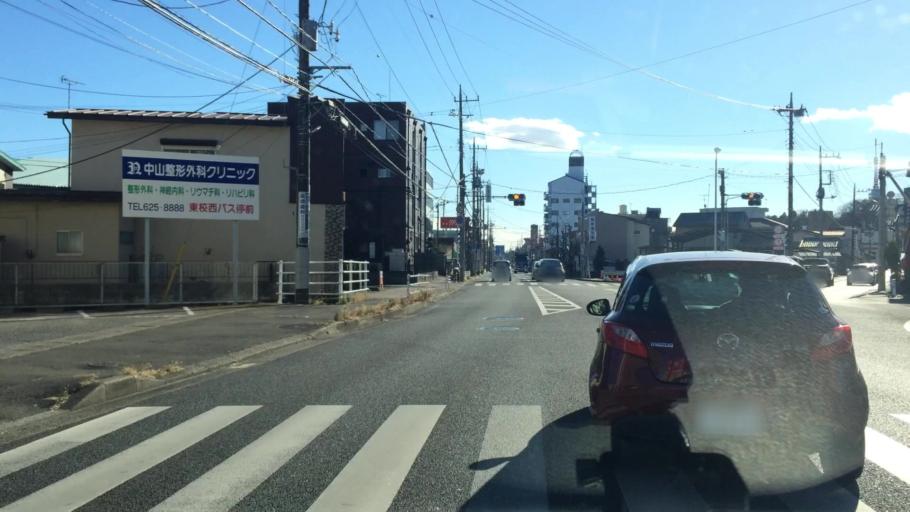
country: JP
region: Tochigi
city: Utsunomiya-shi
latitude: 36.5783
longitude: 139.8901
